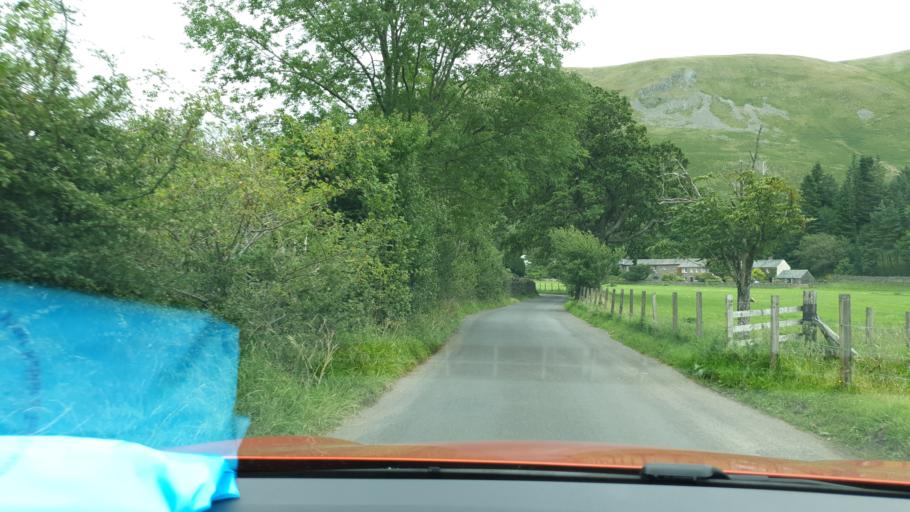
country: GB
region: England
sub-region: Cumbria
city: Penrith
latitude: 54.5682
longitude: -2.8670
